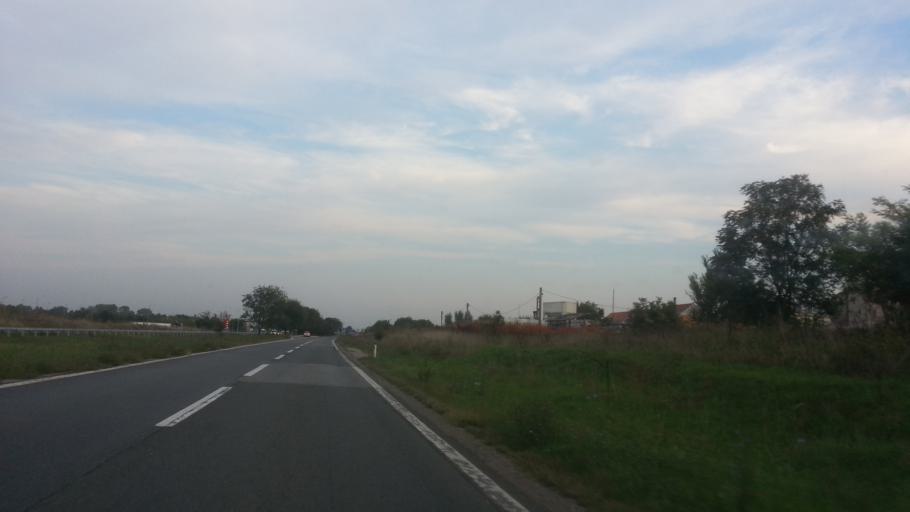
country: RS
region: Central Serbia
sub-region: Belgrade
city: Zemun
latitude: 44.8761
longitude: 20.3278
